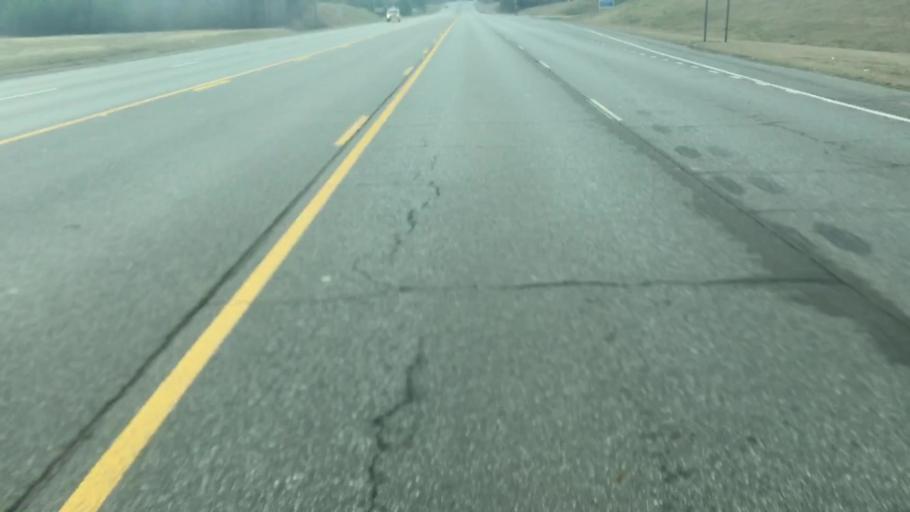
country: US
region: Alabama
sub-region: Walker County
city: Jasper
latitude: 33.8096
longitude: -87.2342
